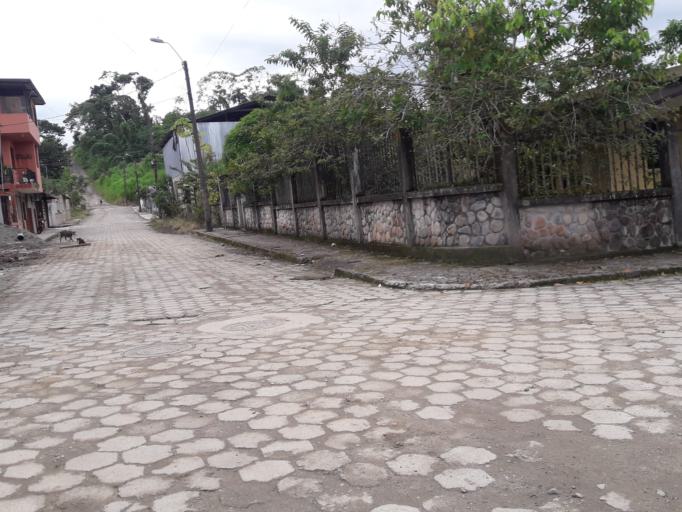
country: EC
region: Napo
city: Tena
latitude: -0.9844
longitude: -77.8170
